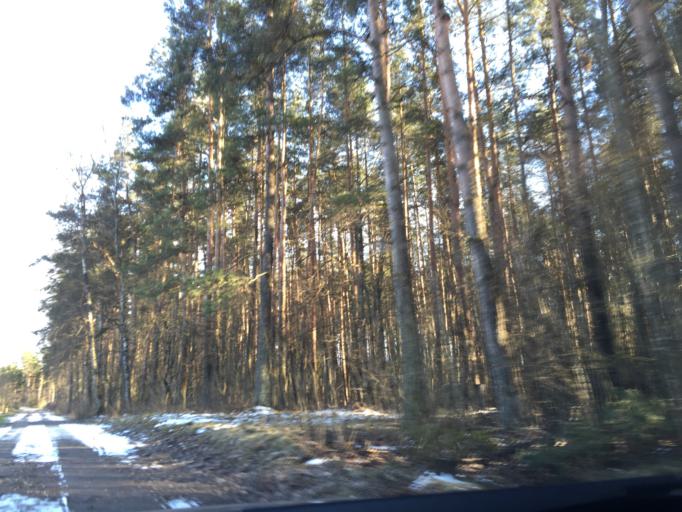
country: LV
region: Kekava
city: Kekava
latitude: 56.8450
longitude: 24.1933
